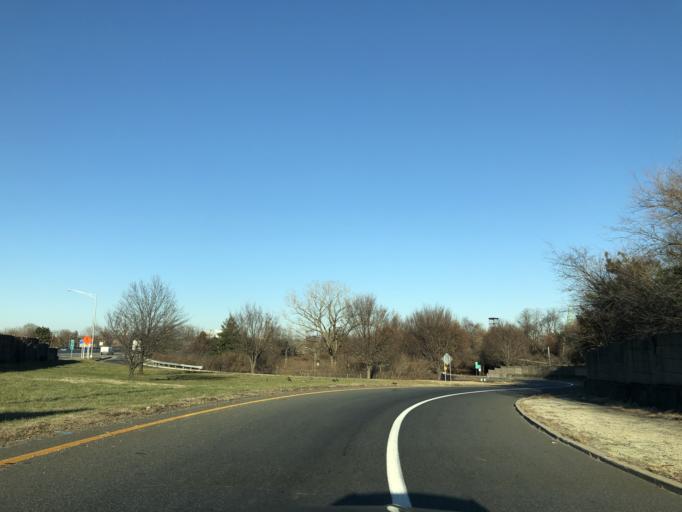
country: US
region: New Jersey
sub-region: Camden County
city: Camden
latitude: 39.9275
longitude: -75.1156
